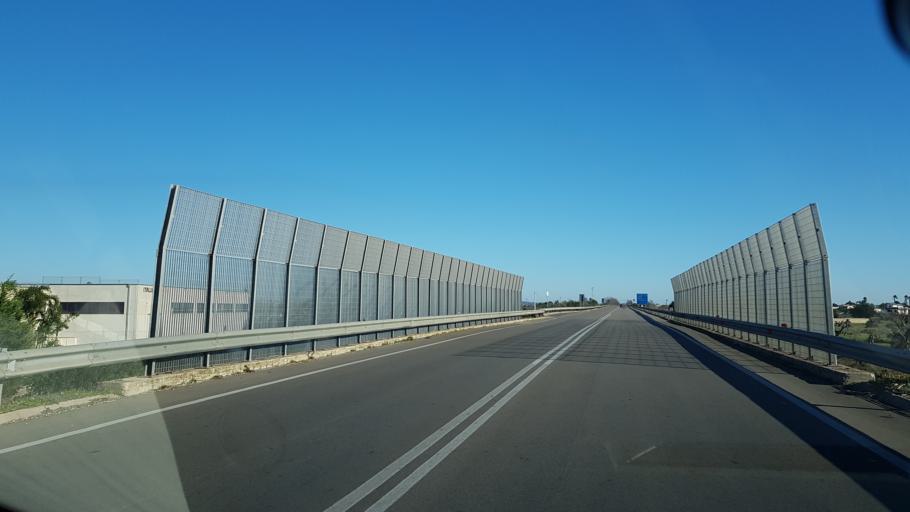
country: IT
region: Apulia
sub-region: Provincia di Lecce
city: Taviano
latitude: 39.9991
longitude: 18.0709
